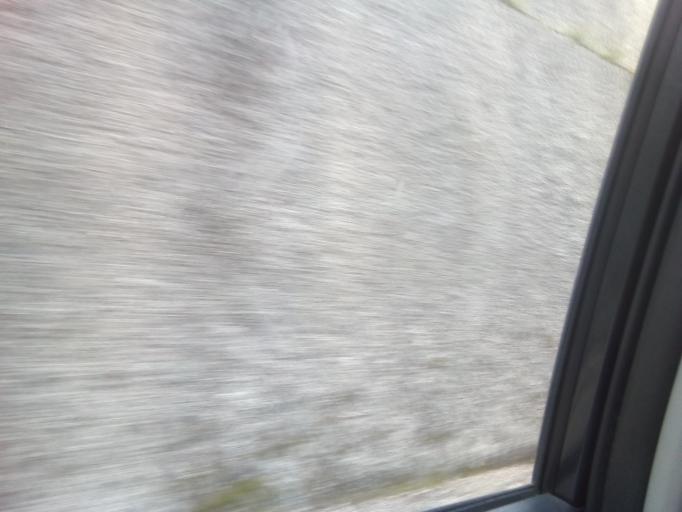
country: IE
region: Munster
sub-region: County Cork
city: Cork
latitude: 51.8931
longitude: -8.4948
